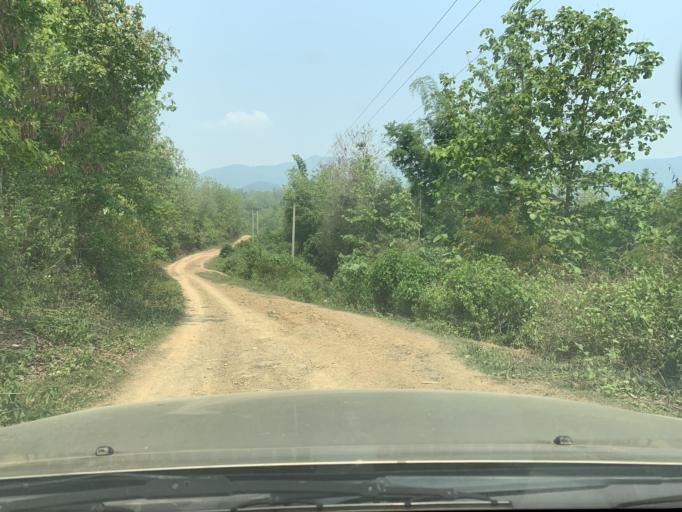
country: LA
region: Louangphabang
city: Louangphabang
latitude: 19.9474
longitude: 102.1337
